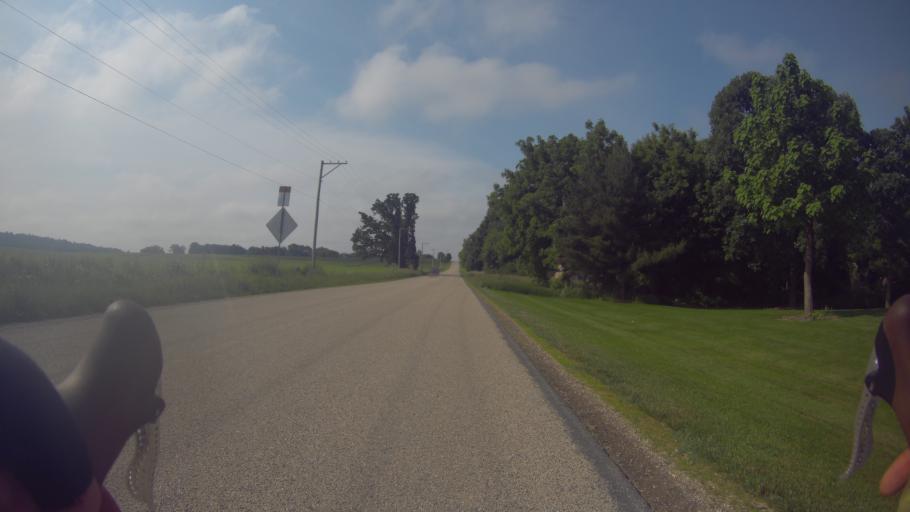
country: US
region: Wisconsin
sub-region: Dane County
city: McFarland
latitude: 43.0115
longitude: -89.2347
